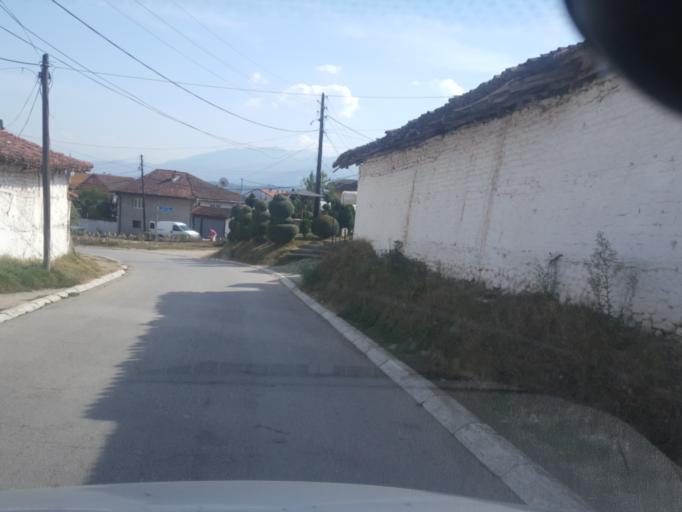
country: XK
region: Gjakova
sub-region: Komuna e Gjakoves
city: Gjakove
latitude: 42.3826
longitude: 20.4234
